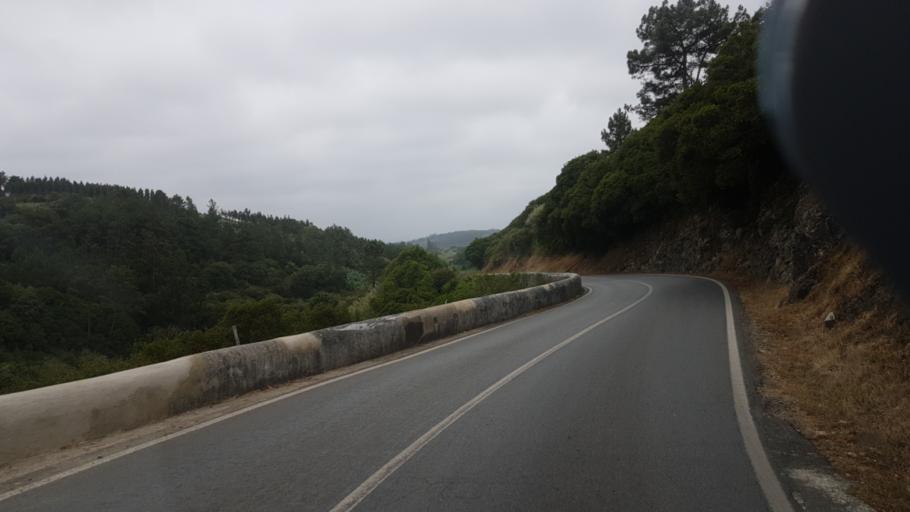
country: PT
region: Leiria
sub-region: Bombarral
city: Bombarral
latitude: 39.2977
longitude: -9.2005
